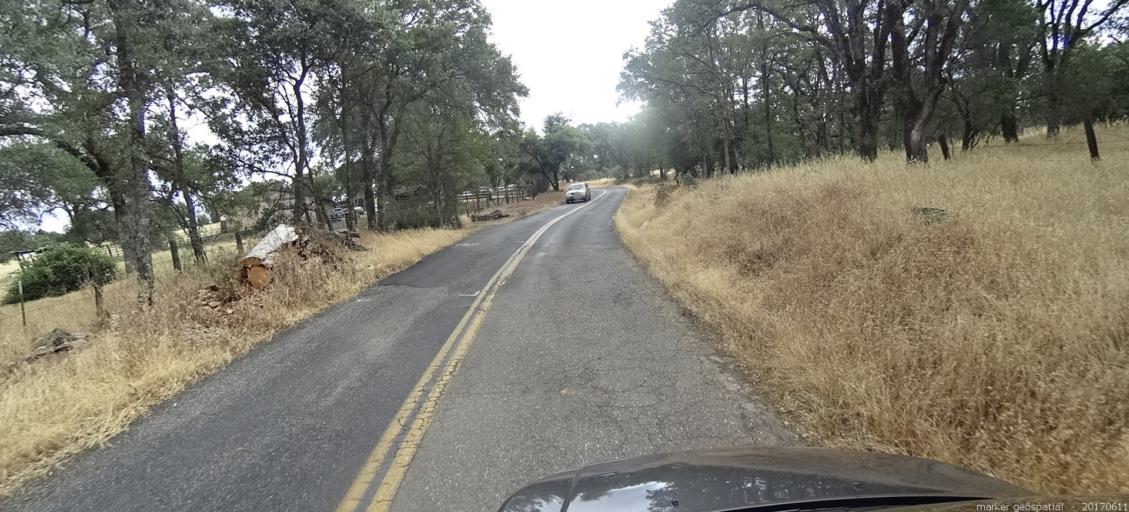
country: US
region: California
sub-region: Butte County
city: Oroville
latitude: 39.6027
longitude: -121.5343
